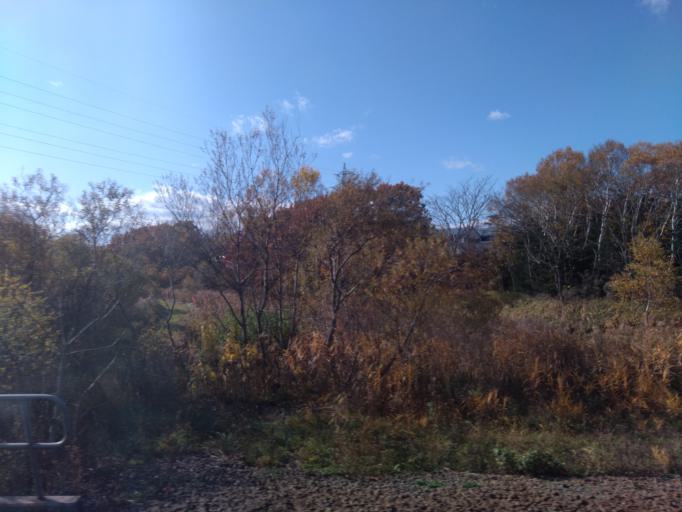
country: JP
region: Hokkaido
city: Kitahiroshima
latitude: 42.9438
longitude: 141.5717
